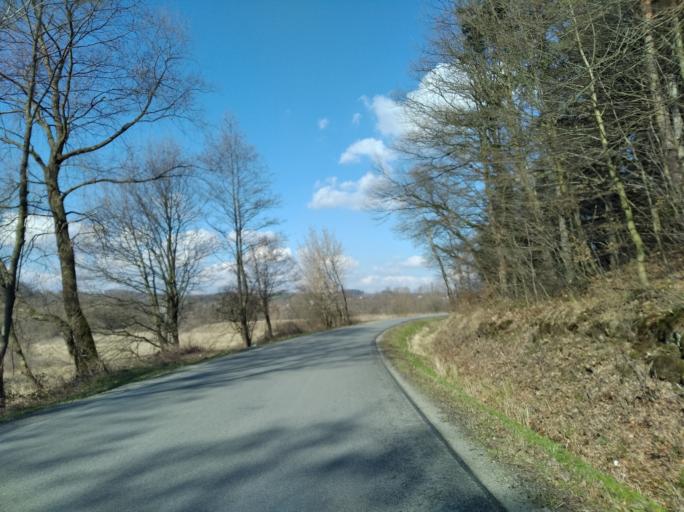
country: PL
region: Subcarpathian Voivodeship
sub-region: Powiat strzyzowski
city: Frysztak
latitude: 49.8536
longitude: 21.6247
